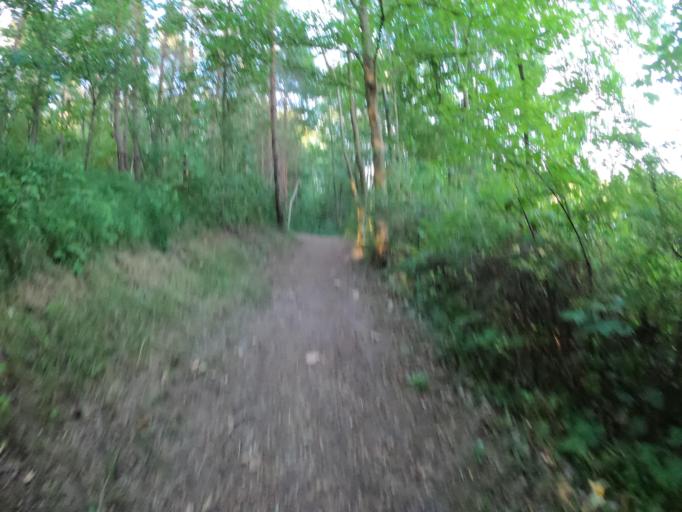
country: DE
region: Brandenburg
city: Templin
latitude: 53.1298
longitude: 13.5247
